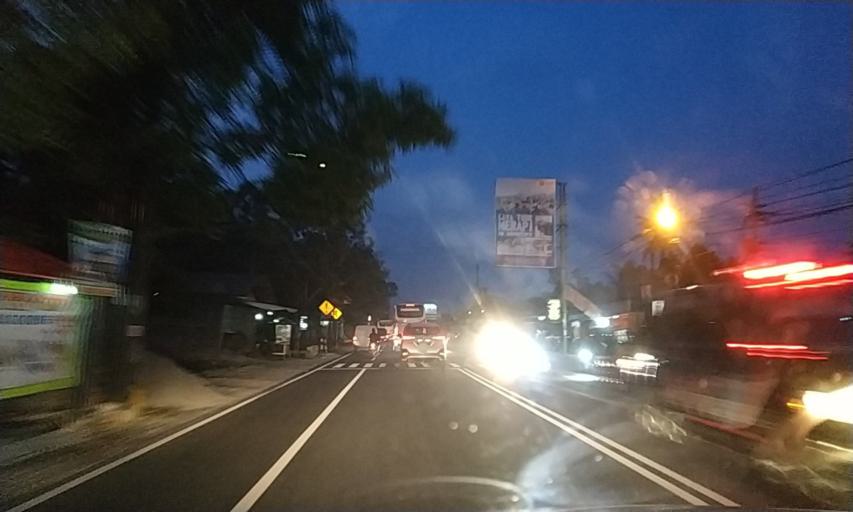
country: ID
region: Daerah Istimewa Yogyakarta
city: Godean
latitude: -7.8088
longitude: 110.2865
